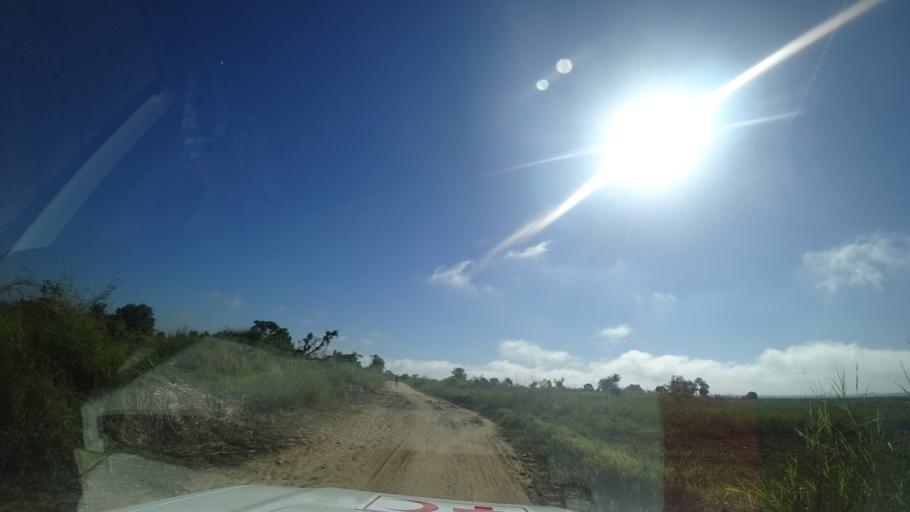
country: MZ
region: Sofala
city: Dondo
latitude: -19.4246
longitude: 34.5624
